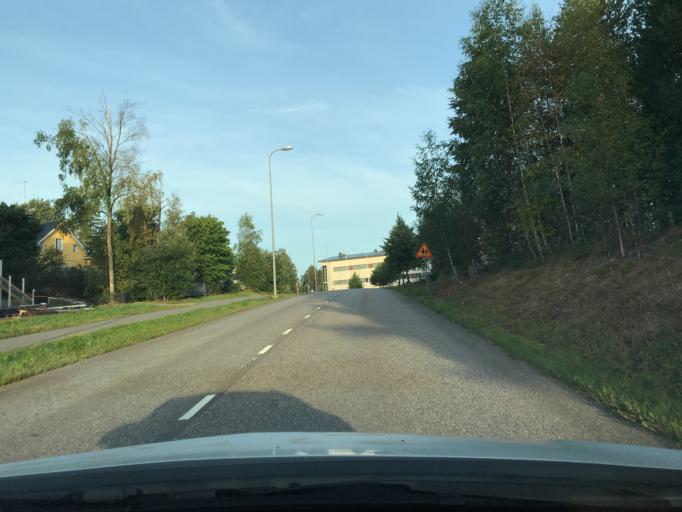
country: FI
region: Uusimaa
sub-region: Helsinki
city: Vihti
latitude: 60.4006
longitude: 24.4827
